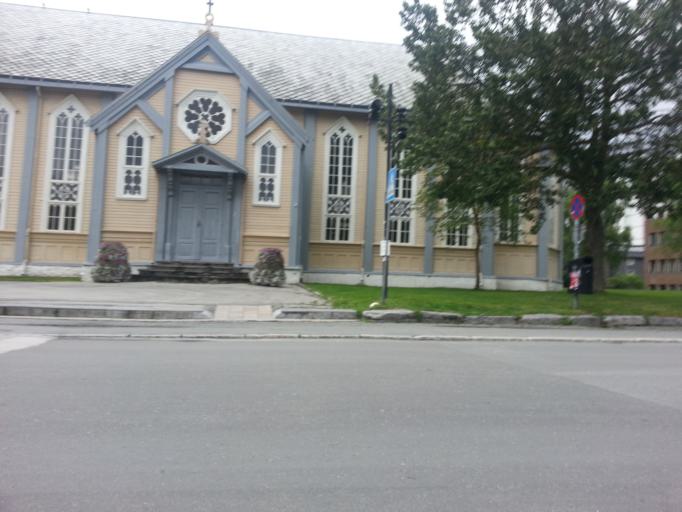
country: NO
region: Troms
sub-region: Tromso
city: Tromso
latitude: 69.6484
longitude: 18.9565
